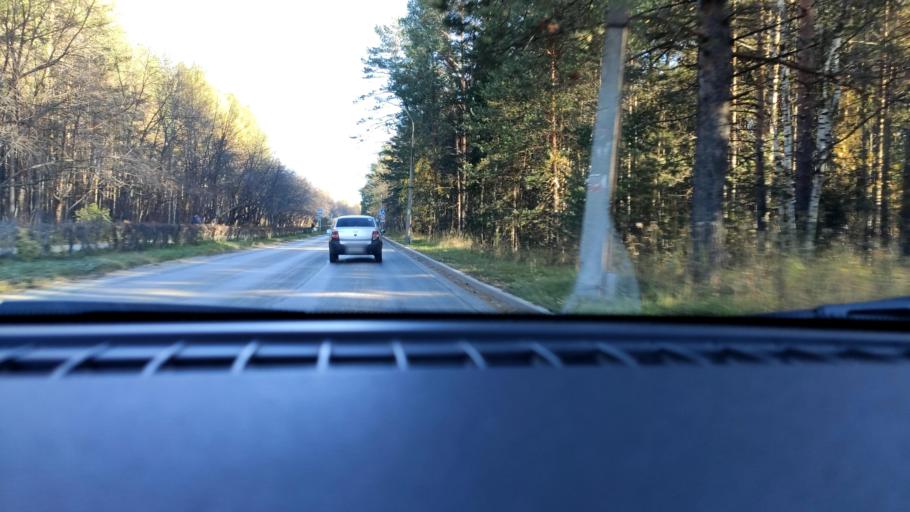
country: RU
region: Perm
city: Perm
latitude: 58.0487
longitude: 56.2131
